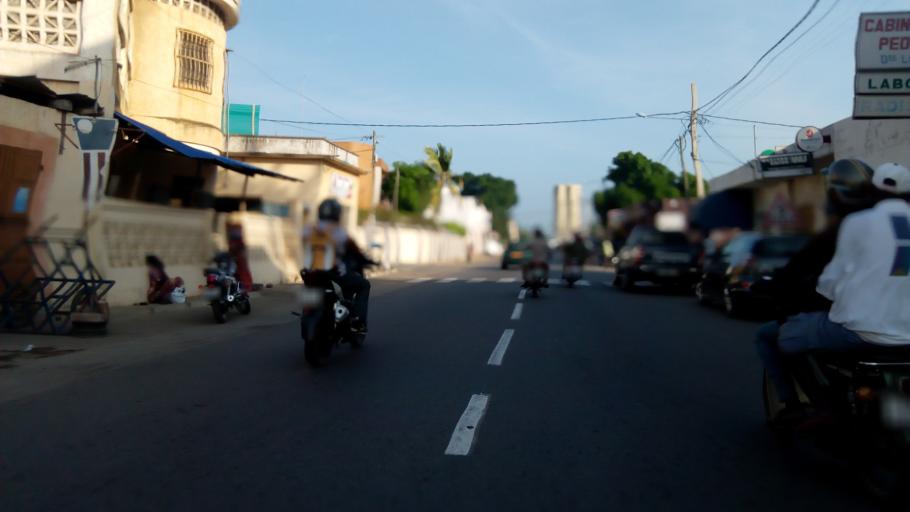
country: TG
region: Maritime
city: Lome
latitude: 6.1341
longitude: 1.2115
